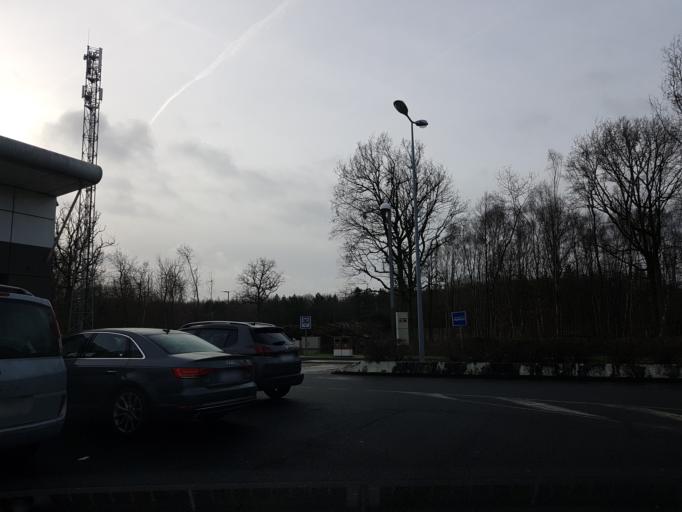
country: FR
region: Ile-de-France
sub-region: Departement de Seine-et-Marne
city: La Grande-Paroisse
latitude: 48.4259
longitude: 2.9276
